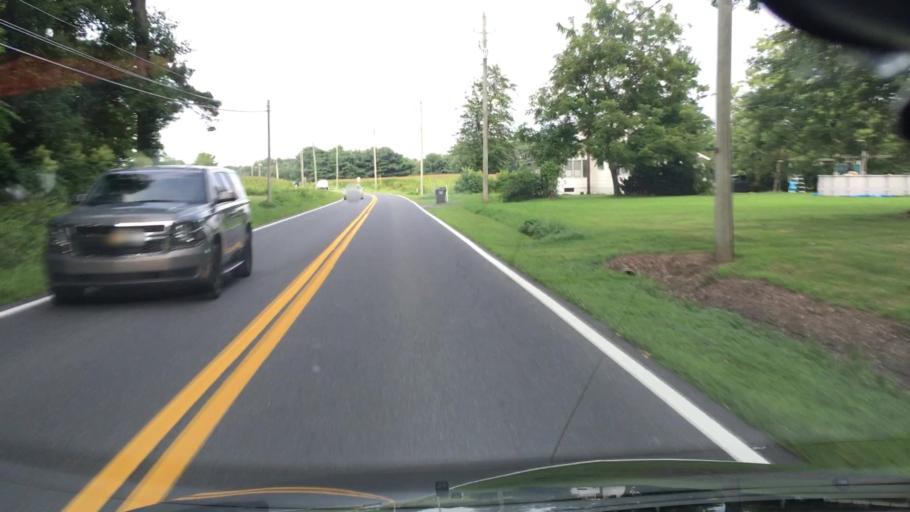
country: US
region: Delaware
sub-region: Sussex County
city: Selbyville
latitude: 38.4386
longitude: -75.1991
